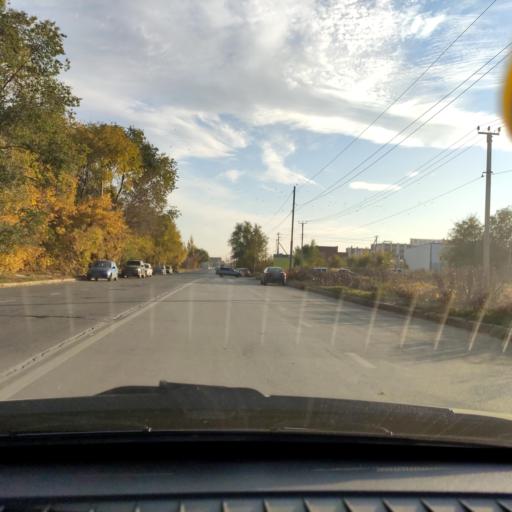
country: RU
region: Samara
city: Tol'yatti
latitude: 53.5633
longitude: 49.2957
